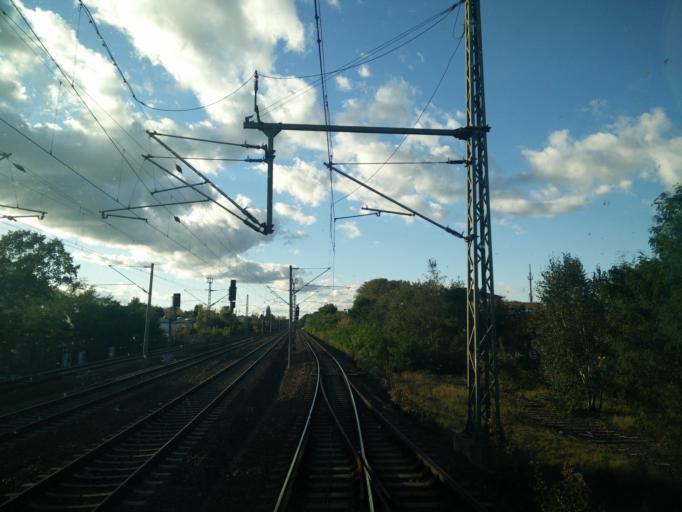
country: DE
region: Brandenburg
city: Falkensee
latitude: 52.5582
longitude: 13.0957
